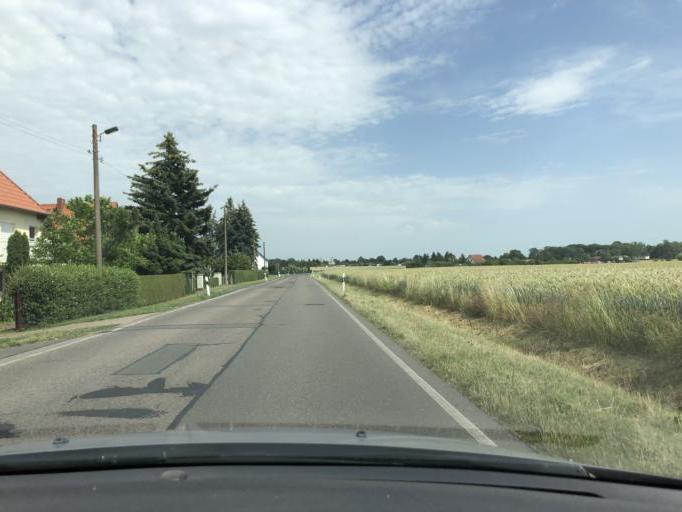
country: DE
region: Saxony
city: Borsdorf
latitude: 51.3682
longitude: 12.5166
